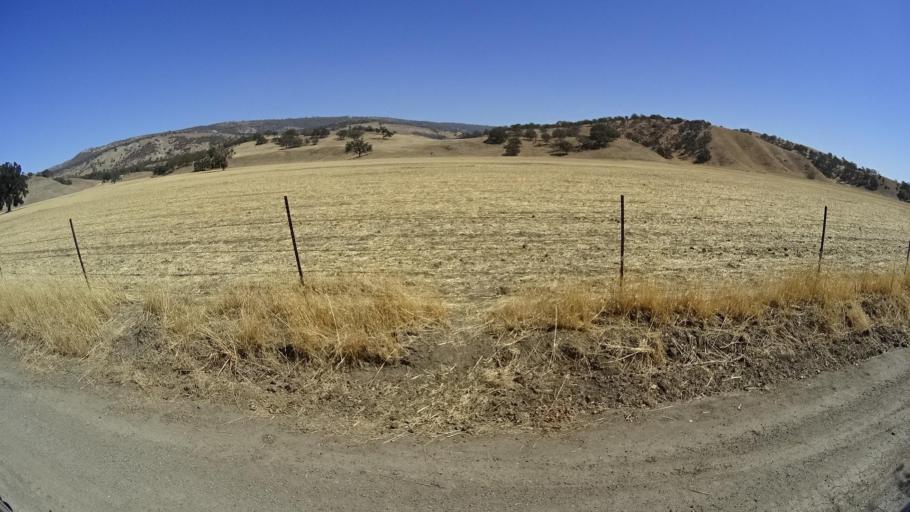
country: US
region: California
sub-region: Fresno County
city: Coalinga
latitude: 35.9033
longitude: -120.4342
